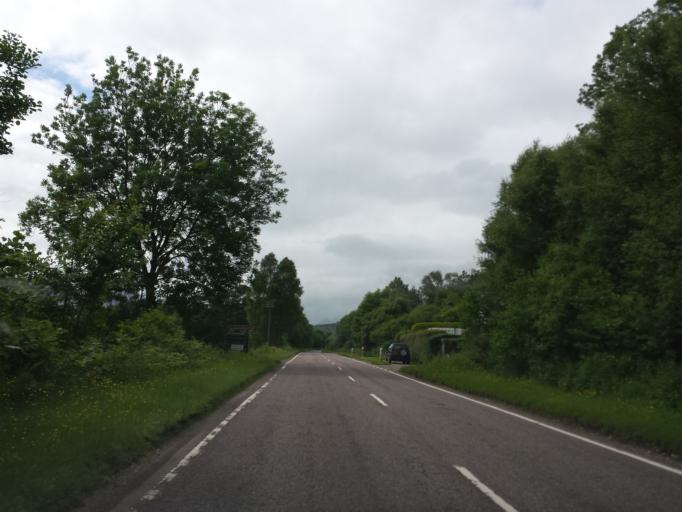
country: GB
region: Scotland
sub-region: Highland
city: Fort William
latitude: 56.8571
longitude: -5.3072
